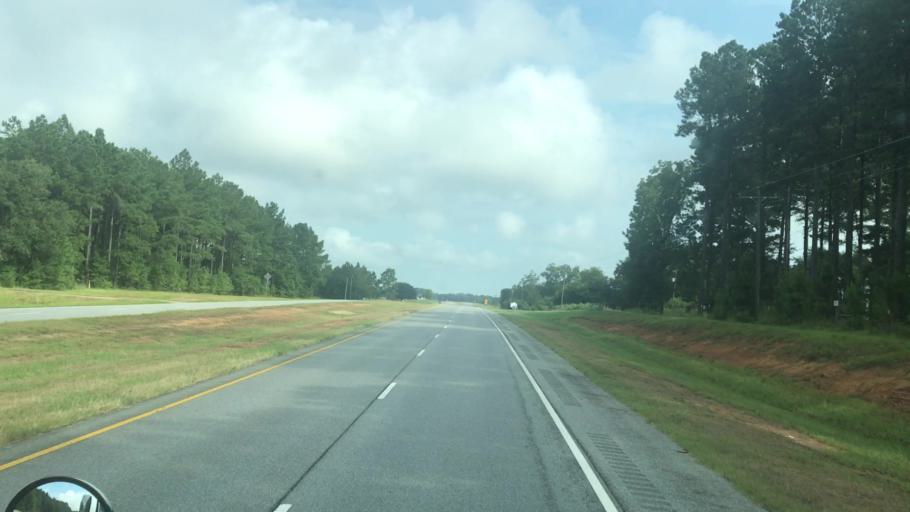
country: US
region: Georgia
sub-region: Miller County
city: Colquitt
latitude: 31.2292
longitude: -84.7820
